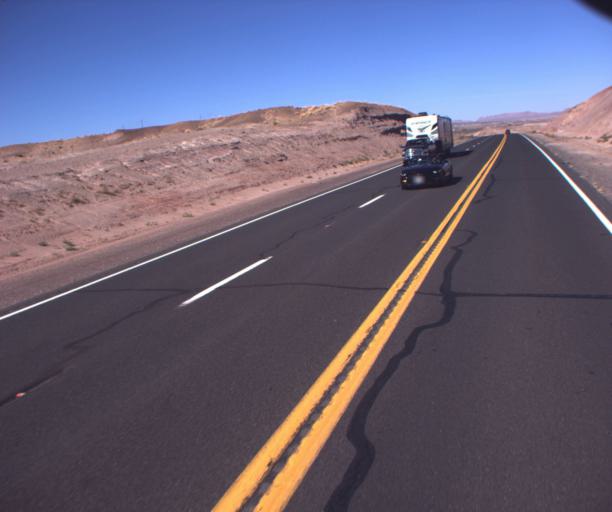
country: US
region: Arizona
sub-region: Coconino County
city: Tuba City
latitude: 35.9944
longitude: -111.3929
